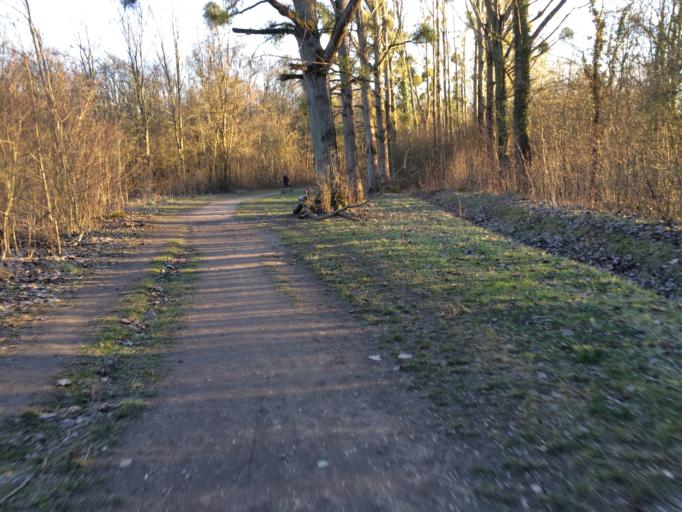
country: FR
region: Ile-de-France
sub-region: Departement de l'Essonne
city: Villebon-sur-Yvette
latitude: 48.7138
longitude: 2.2217
